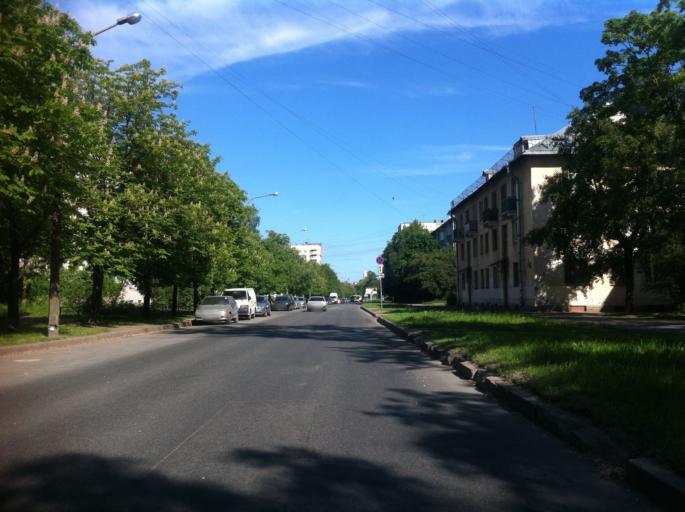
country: RU
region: St.-Petersburg
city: Dachnoye
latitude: 59.8393
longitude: 30.2491
